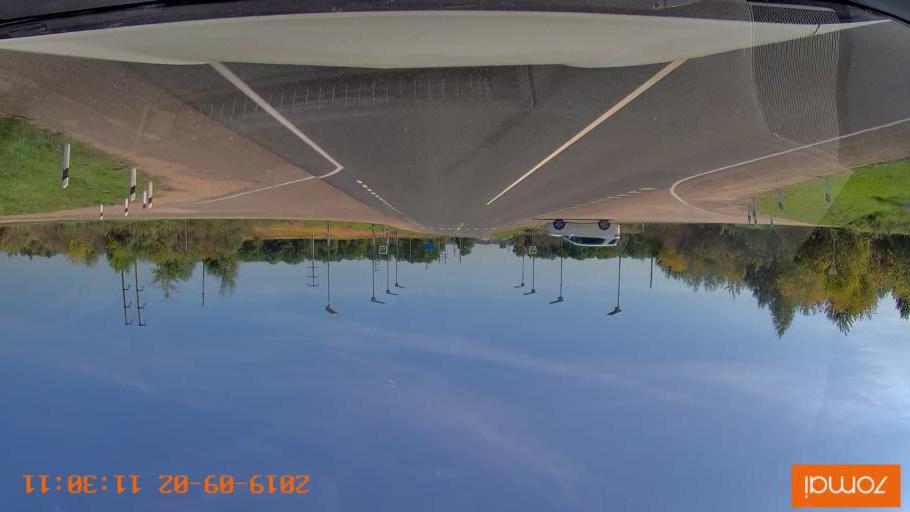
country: RU
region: Smolensk
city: Roslavl'
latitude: 53.9864
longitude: 32.8398
